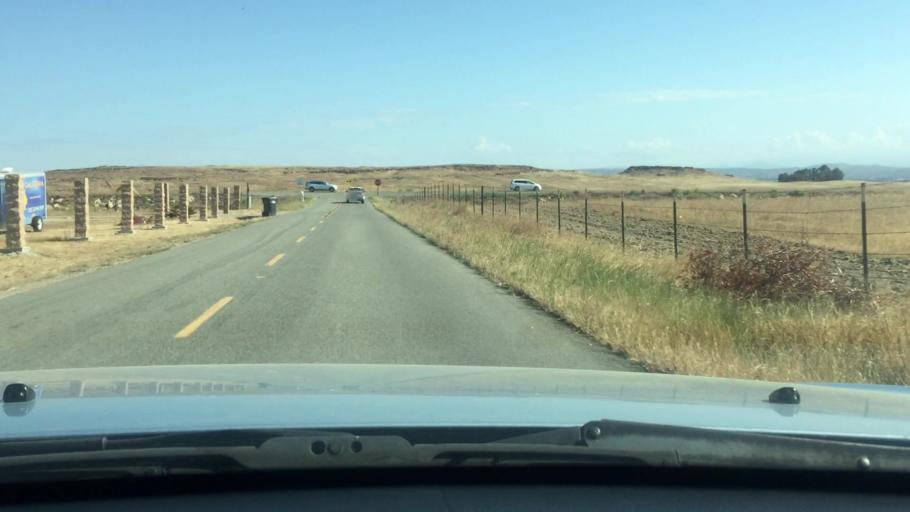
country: US
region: California
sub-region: Madera County
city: Bonadelle Ranchos-Madera Ranchos
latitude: 37.0090
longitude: -119.8576
